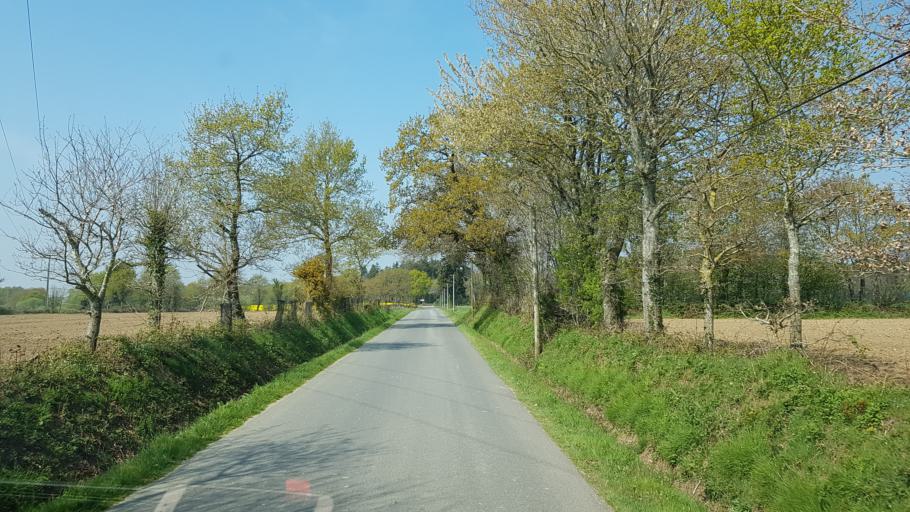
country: FR
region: Brittany
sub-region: Departement du Morbihan
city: Peaule
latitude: 47.5877
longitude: -2.3909
